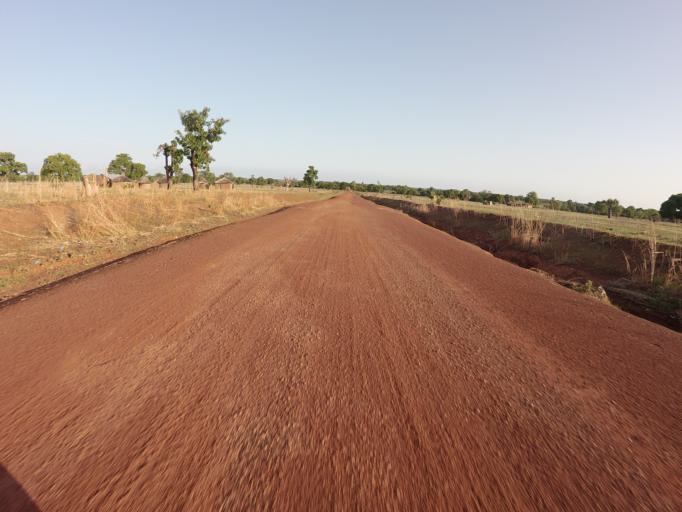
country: TG
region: Savanes
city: Sansanne-Mango
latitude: 10.3522
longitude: -0.0930
